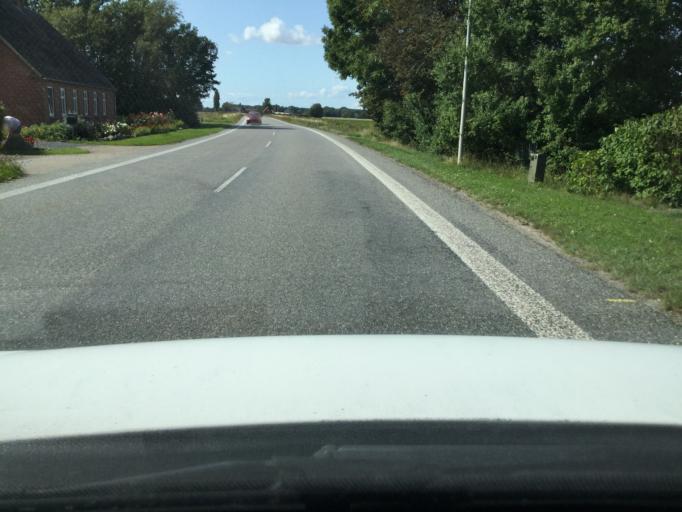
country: DK
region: Zealand
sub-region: Lolland Kommune
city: Rodby
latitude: 54.7500
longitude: 11.3816
